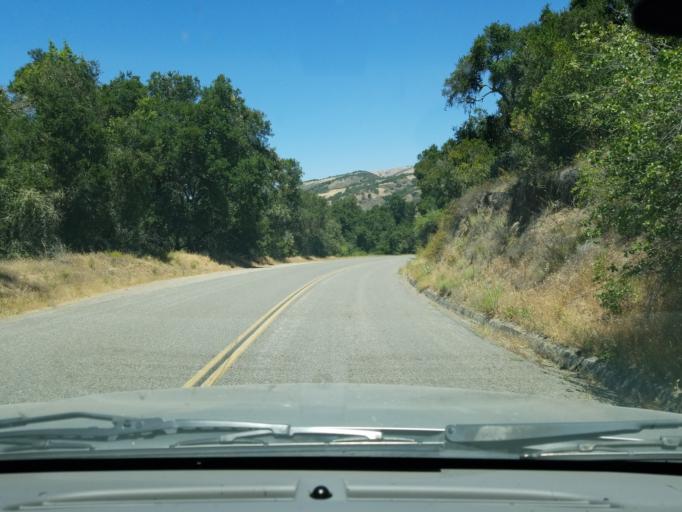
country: US
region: California
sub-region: Monterey County
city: Chualar
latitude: 36.4092
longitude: -121.5934
